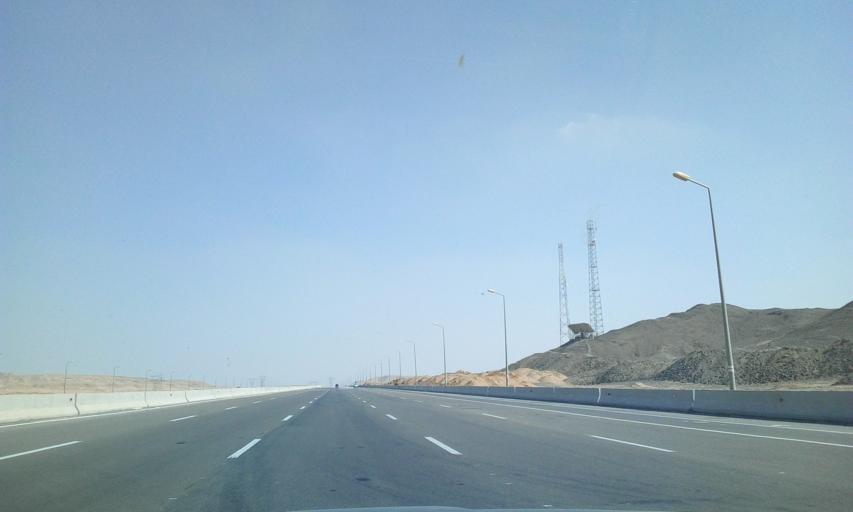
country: EG
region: As Suways
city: Ain Sukhna
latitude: 29.8713
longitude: 31.8535
